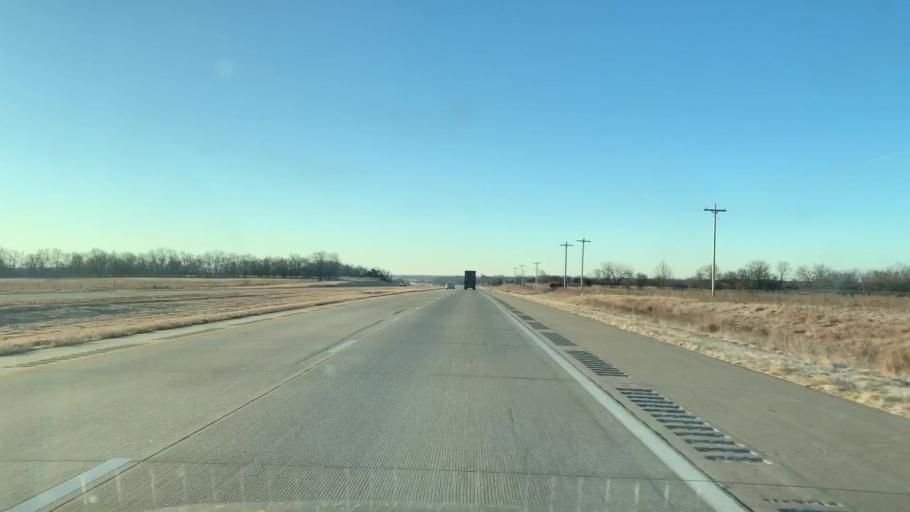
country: US
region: Kansas
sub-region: Linn County
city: Pleasanton
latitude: 38.0914
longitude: -94.7137
